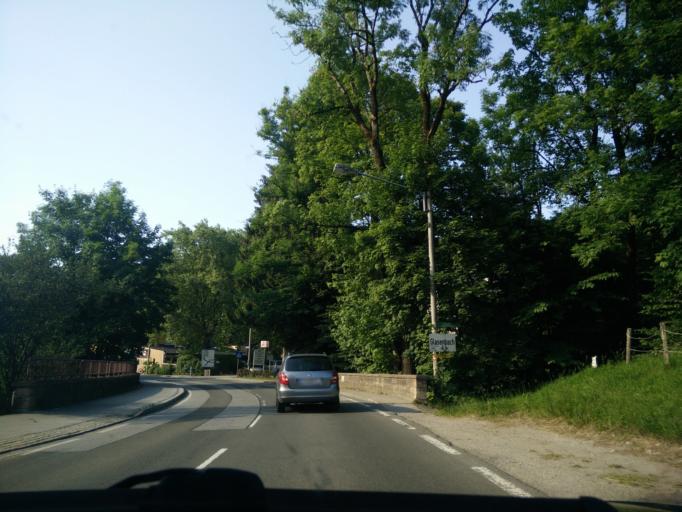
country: AT
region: Salzburg
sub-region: Politischer Bezirk Salzburg-Umgebung
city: Elsbethen
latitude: 47.7685
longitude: 13.0897
